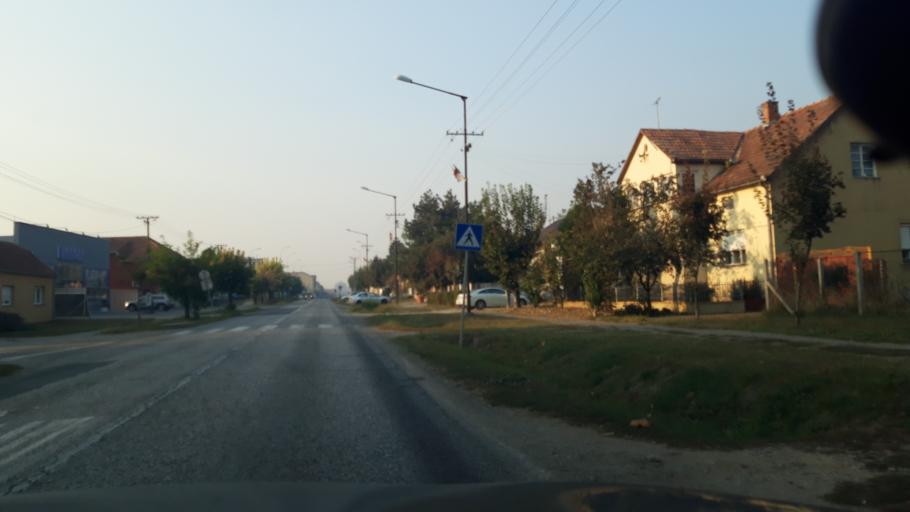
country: RS
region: Autonomna Pokrajina Vojvodina
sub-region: Sremski Okrug
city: Ingija
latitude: 45.0387
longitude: 20.0906
